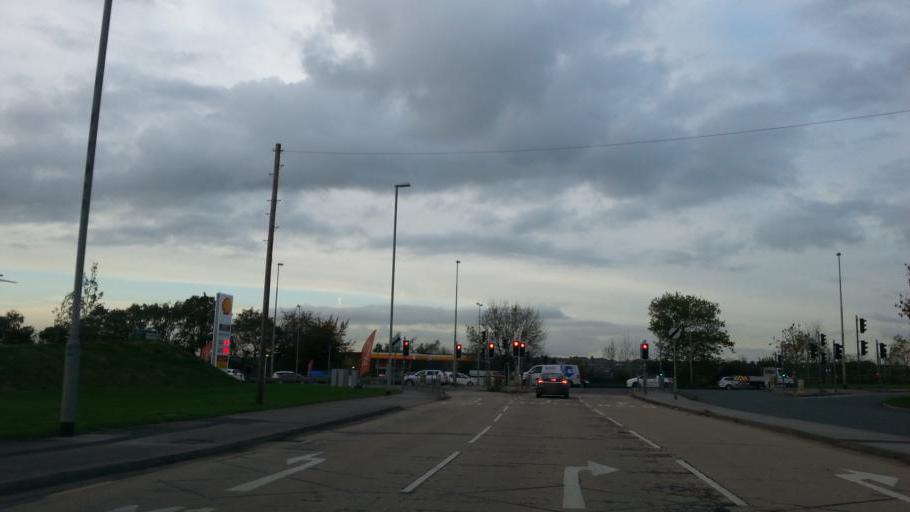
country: GB
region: England
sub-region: Derbyshire
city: Pinxton
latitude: 53.1108
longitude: -1.2966
